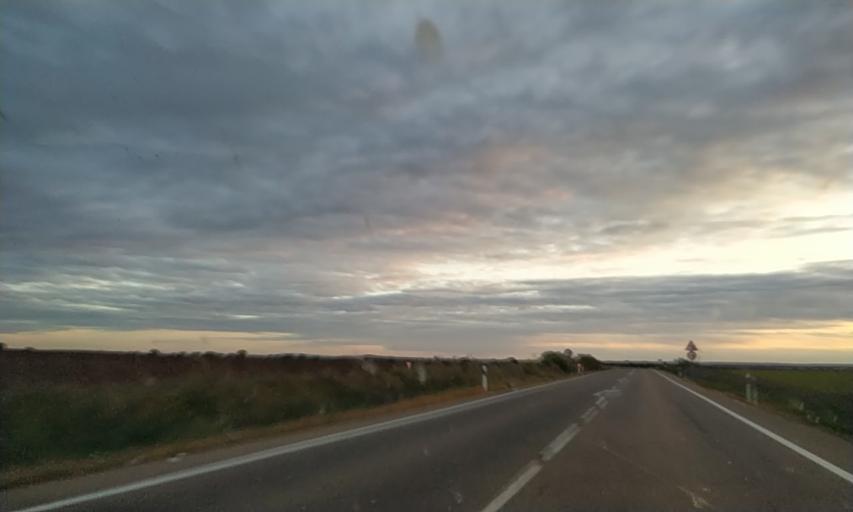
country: ES
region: Extremadura
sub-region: Provincia de Badajoz
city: Villar del Rey
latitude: 39.0541
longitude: -6.7951
